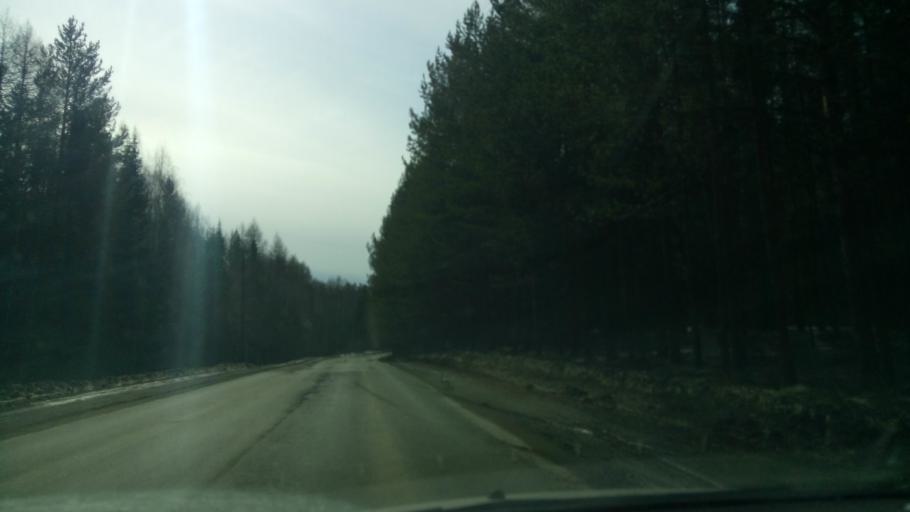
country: RU
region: Sverdlovsk
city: Chernoistochinsk
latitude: 57.7139
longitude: 59.7835
